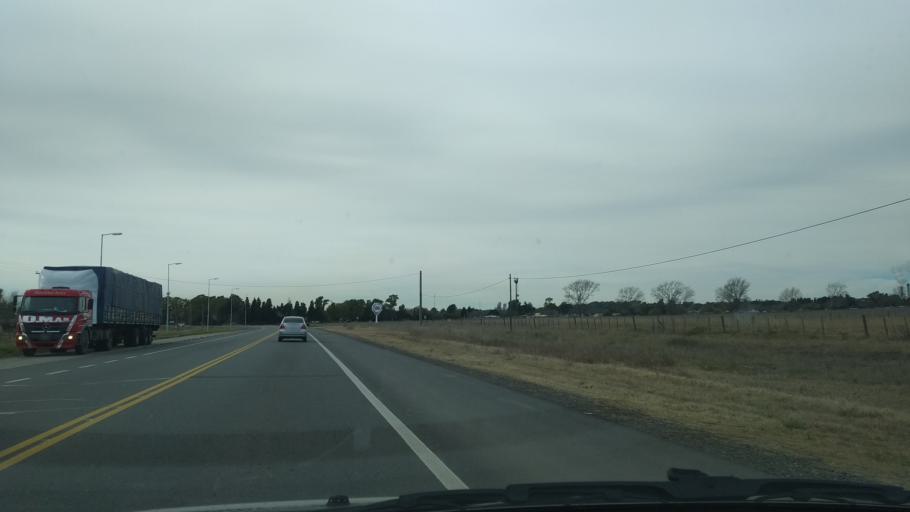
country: AR
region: Buenos Aires
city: Olavarria
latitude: -36.9850
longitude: -60.2939
